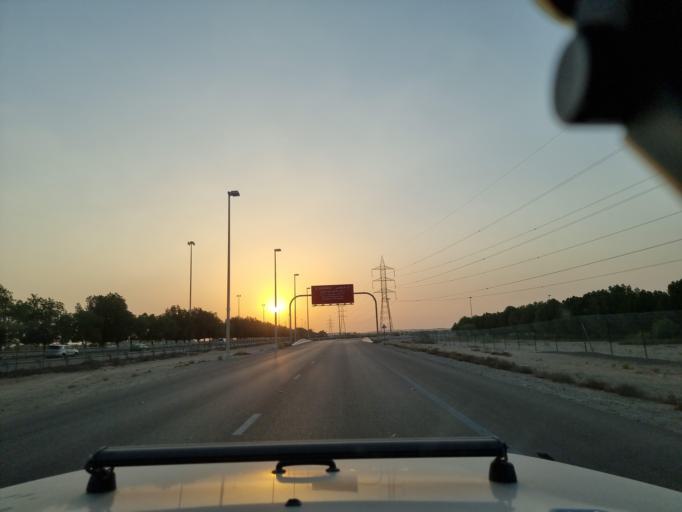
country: AE
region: Abu Dhabi
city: Abu Dhabi
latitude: 24.1922
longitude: 54.9919
